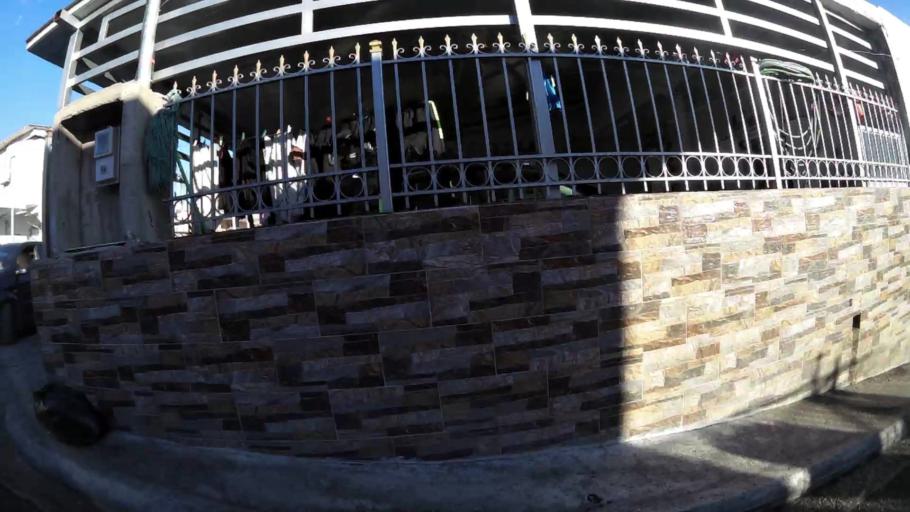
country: GR
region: Attica
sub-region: Nomarchia Anatolikis Attikis
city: Acharnes
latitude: 38.0761
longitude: 23.7245
